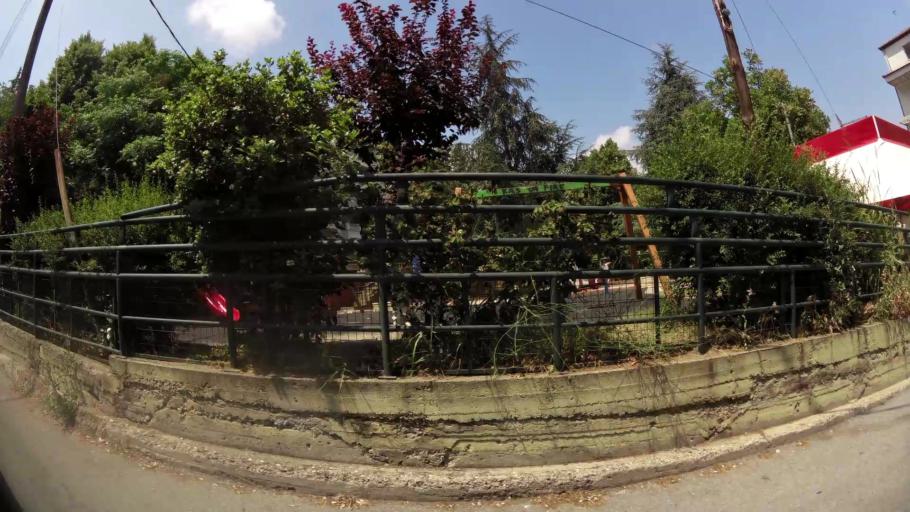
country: GR
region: Central Macedonia
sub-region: Nomos Imathias
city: Veroia
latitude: 40.5110
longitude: 22.2063
